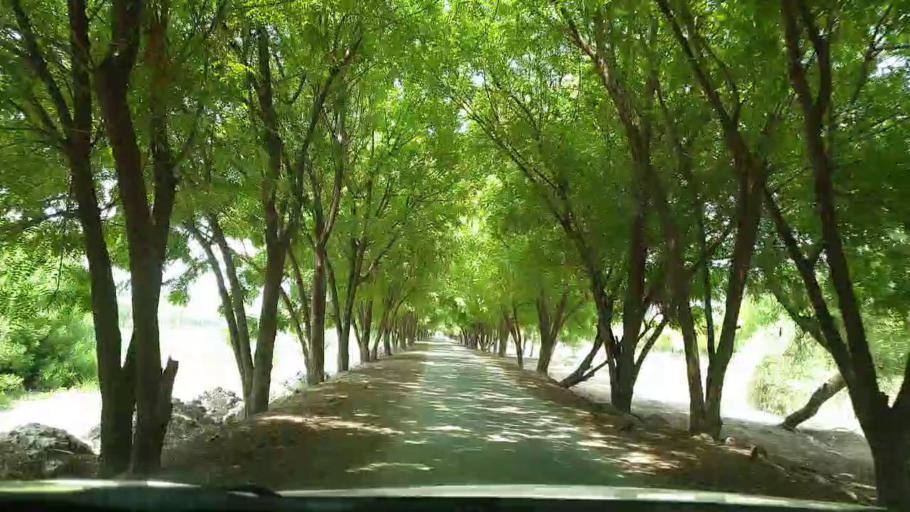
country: PK
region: Sindh
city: Dokri
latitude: 27.3606
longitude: 68.1138
